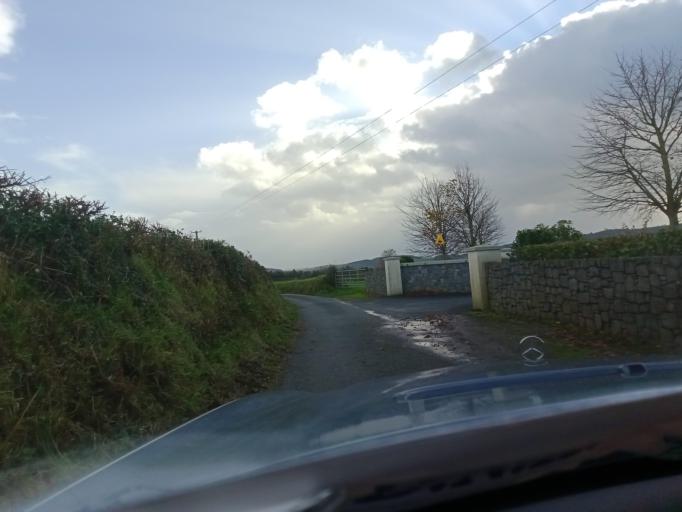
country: IE
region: Leinster
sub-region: Kilkenny
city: Mooncoin
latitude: 52.2871
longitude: -7.2711
